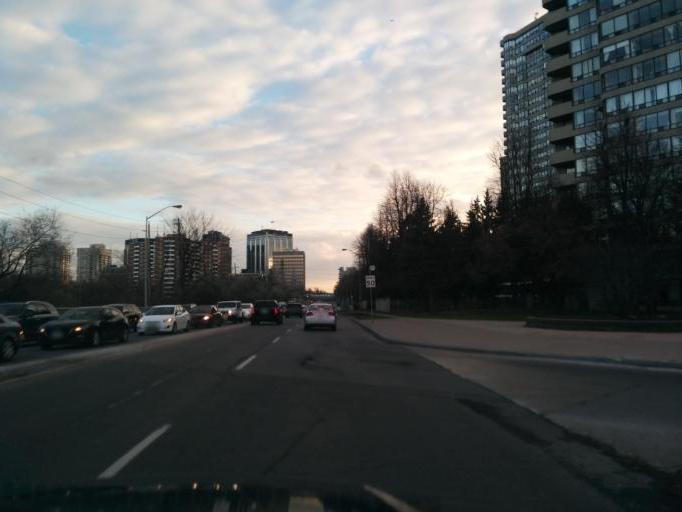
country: CA
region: Ontario
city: Etobicoke
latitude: 43.6512
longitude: -79.5264
